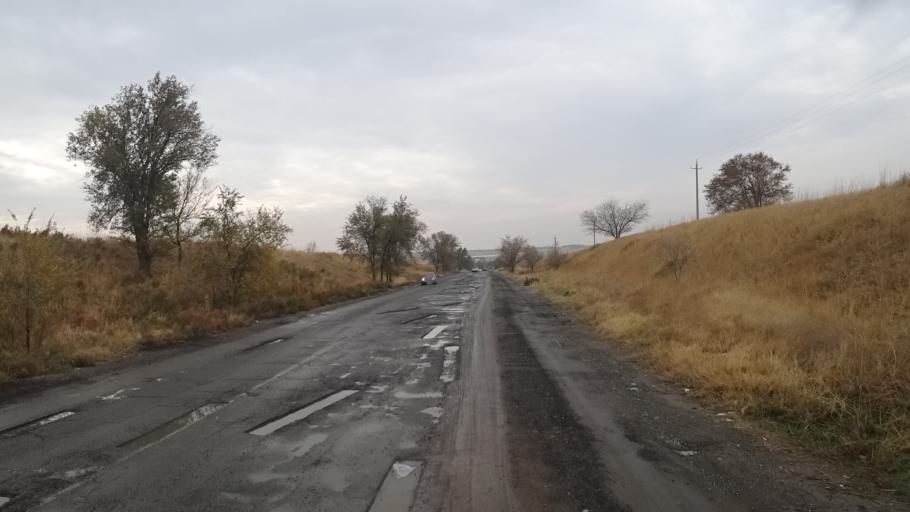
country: KZ
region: Ongtustik Qazaqstan
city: Aksu
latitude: 42.4302
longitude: 69.7101
